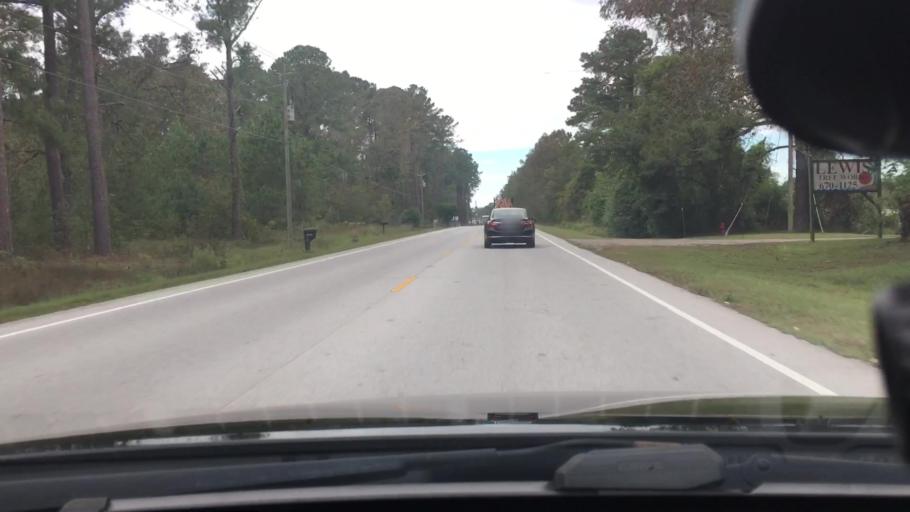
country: US
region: North Carolina
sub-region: Craven County
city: New Bern
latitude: 35.2132
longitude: -77.0625
